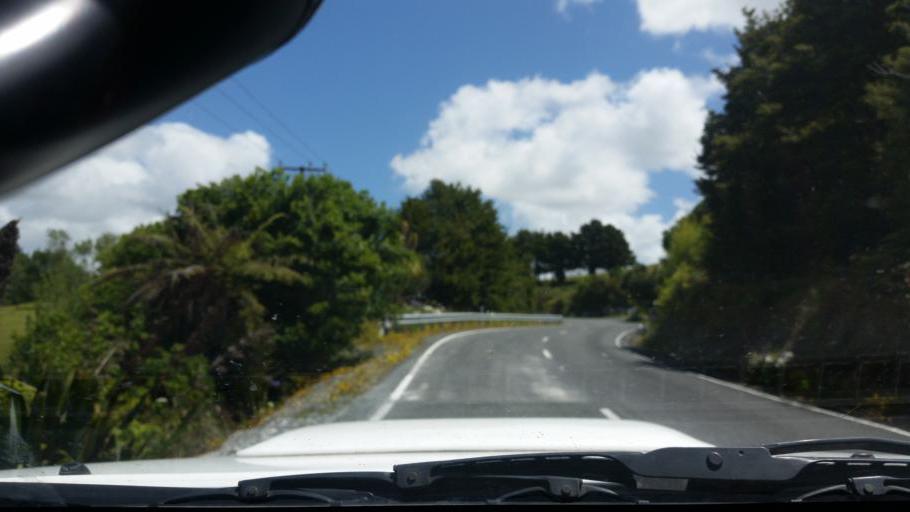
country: NZ
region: Northland
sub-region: Whangarei
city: Ruakaka
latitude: -36.0654
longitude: 174.2664
